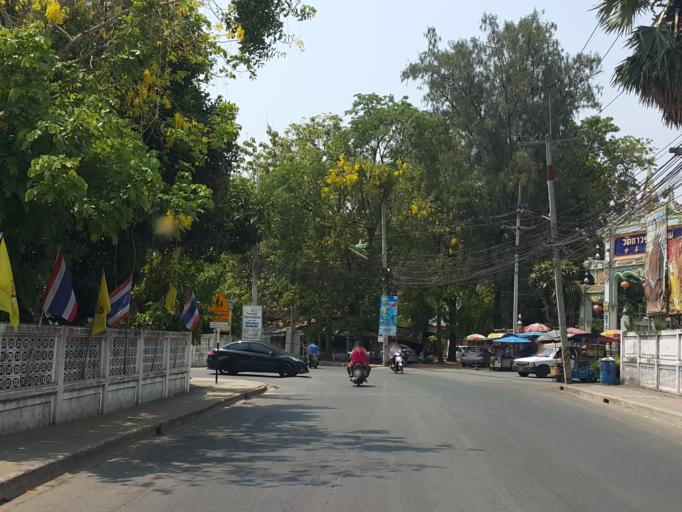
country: TH
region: Kanchanaburi
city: Kanchanaburi
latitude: 14.0294
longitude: 99.5260
